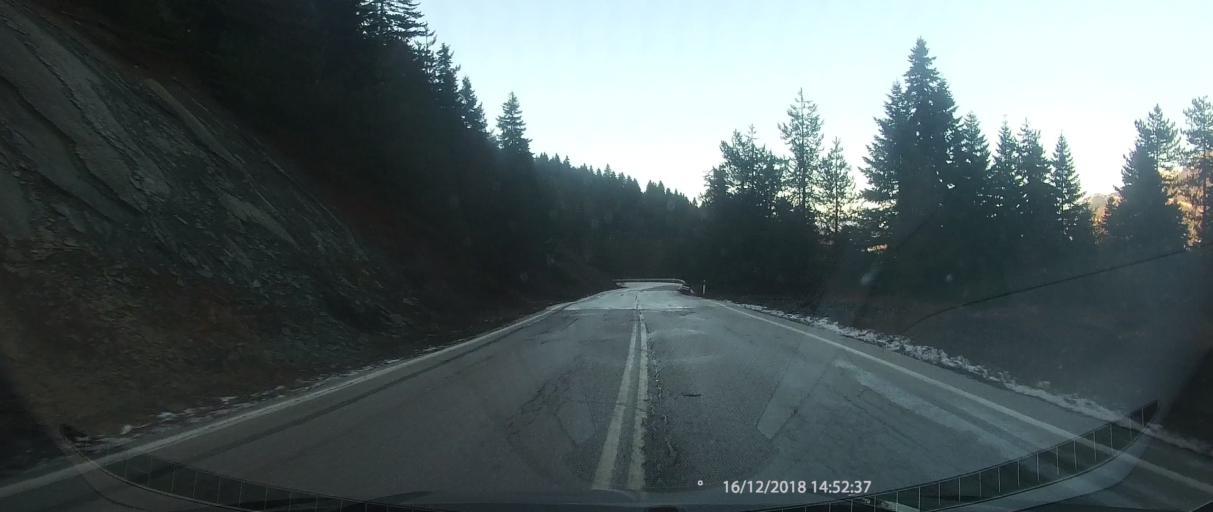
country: GR
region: West Macedonia
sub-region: Nomos Kastorias
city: Nestorio
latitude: 40.2053
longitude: 21.0604
